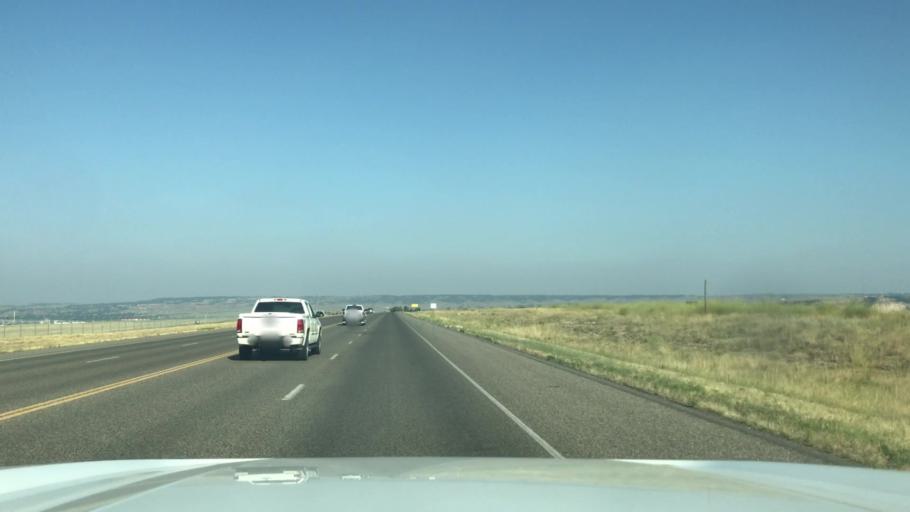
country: US
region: Montana
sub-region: Yellowstone County
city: Billings
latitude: 45.8001
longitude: -108.5168
